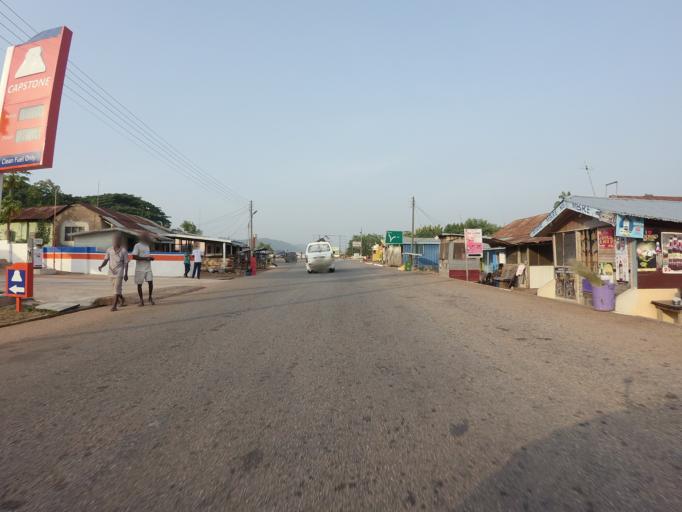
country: GH
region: Volta
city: Ho
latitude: 6.5707
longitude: 0.3050
